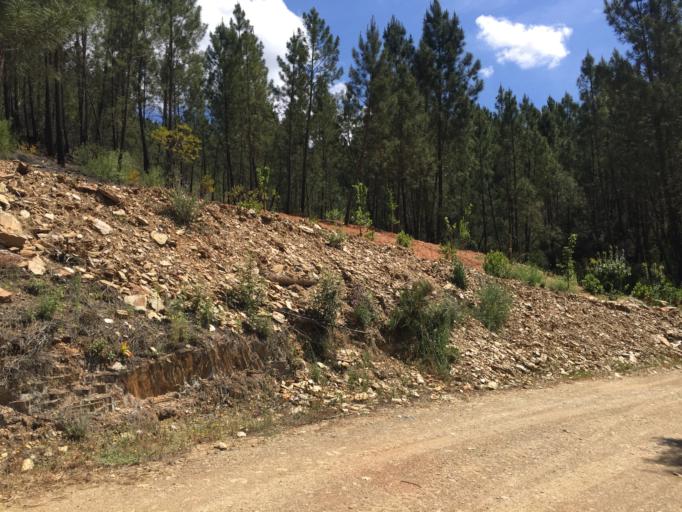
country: PT
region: Coimbra
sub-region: Pampilhosa da Serra
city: Pampilhosa da Serra
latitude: 40.0707
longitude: -7.7813
